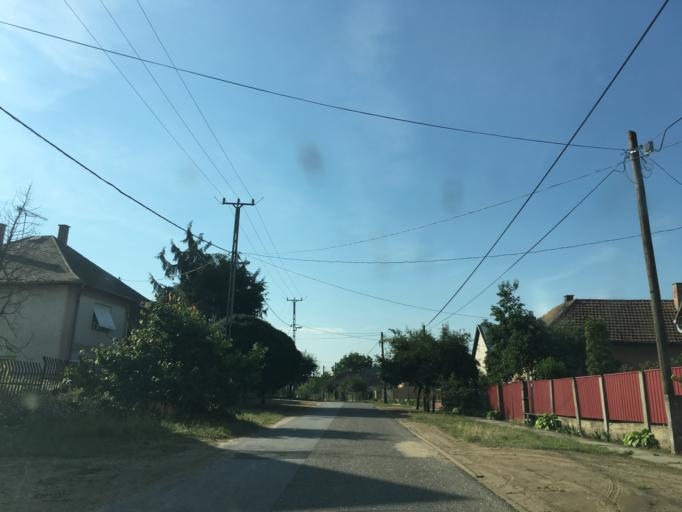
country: HU
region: Szabolcs-Szatmar-Bereg
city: Nyirbeltek
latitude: 47.6921
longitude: 22.1311
